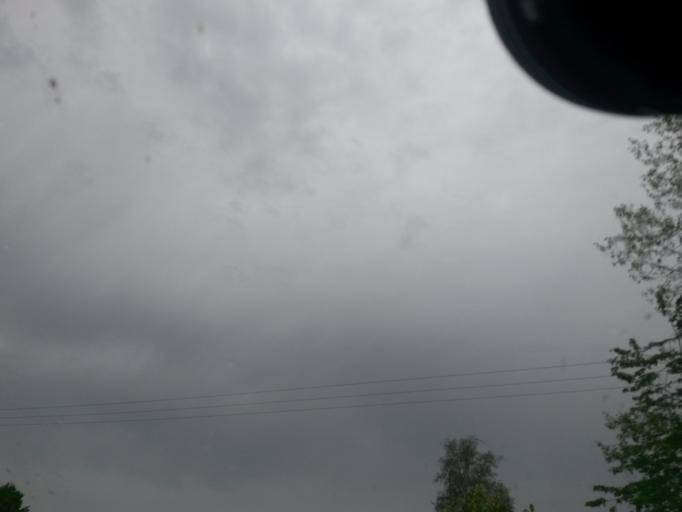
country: DE
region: Bavaria
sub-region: Upper Franconia
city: Forchheim
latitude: 49.7209
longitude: 11.0513
